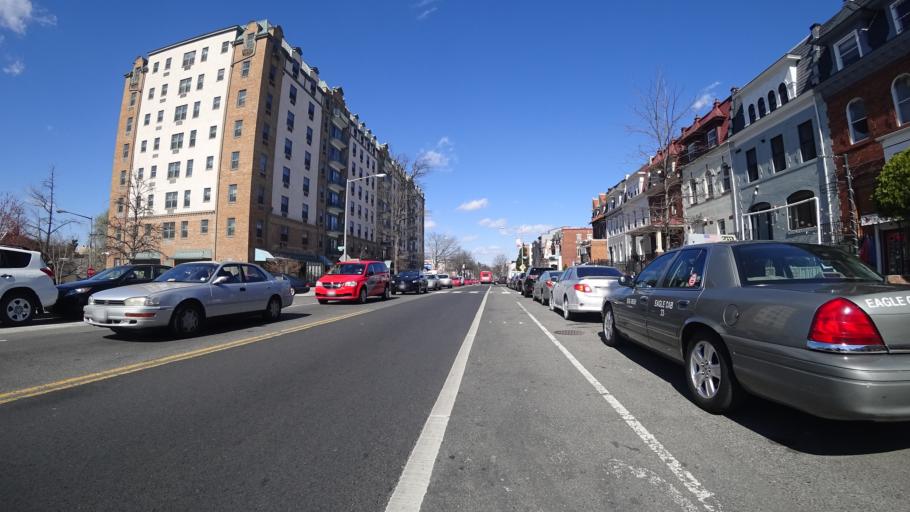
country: US
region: Washington, D.C.
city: Washington, D.C.
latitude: 38.9339
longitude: -77.0327
